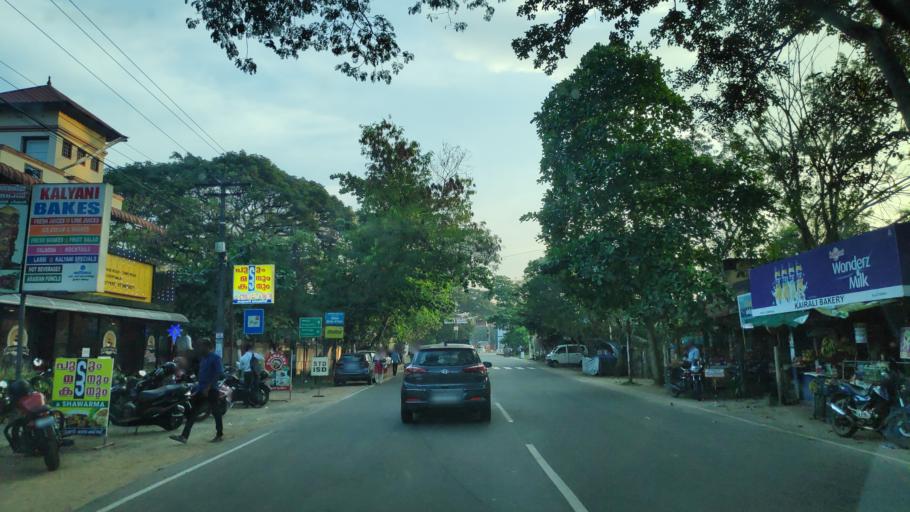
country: IN
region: Kerala
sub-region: Alappuzha
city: Shertallai
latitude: 9.6753
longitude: 76.3405
